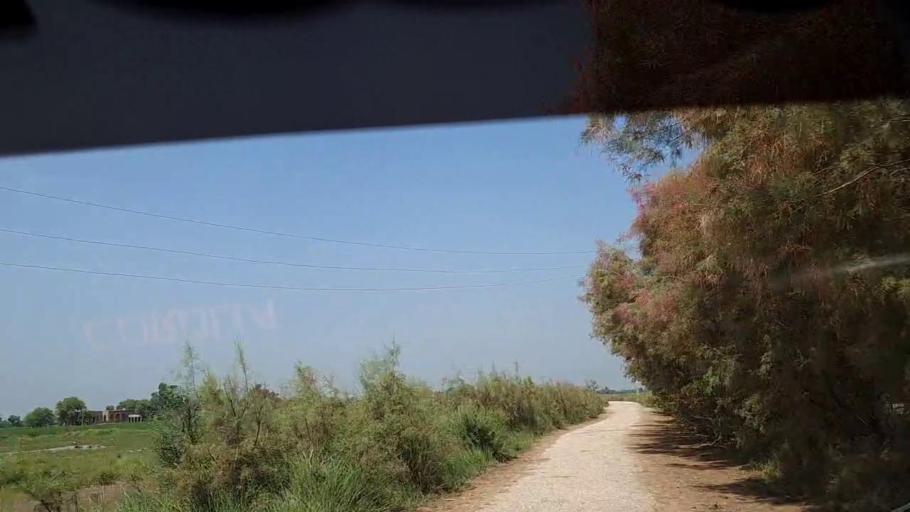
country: PK
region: Sindh
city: Ghauspur
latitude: 28.1710
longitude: 69.0691
